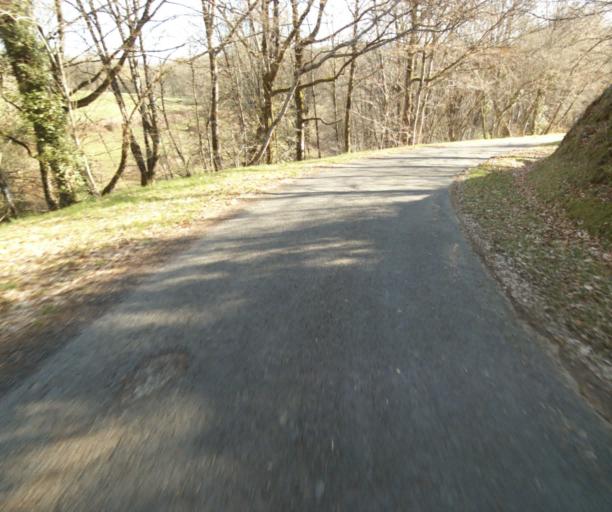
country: FR
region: Limousin
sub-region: Departement de la Correze
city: Seilhac
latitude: 45.3592
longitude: 1.7520
